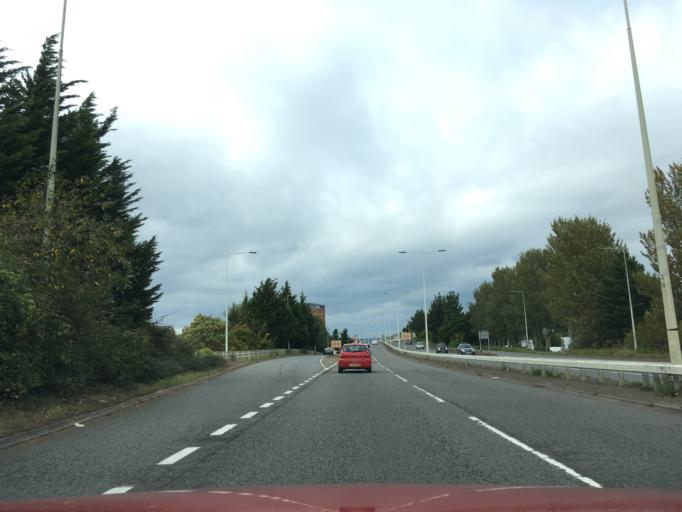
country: GB
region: Wales
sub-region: Cardiff
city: Cardiff
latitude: 51.4745
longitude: -3.1633
